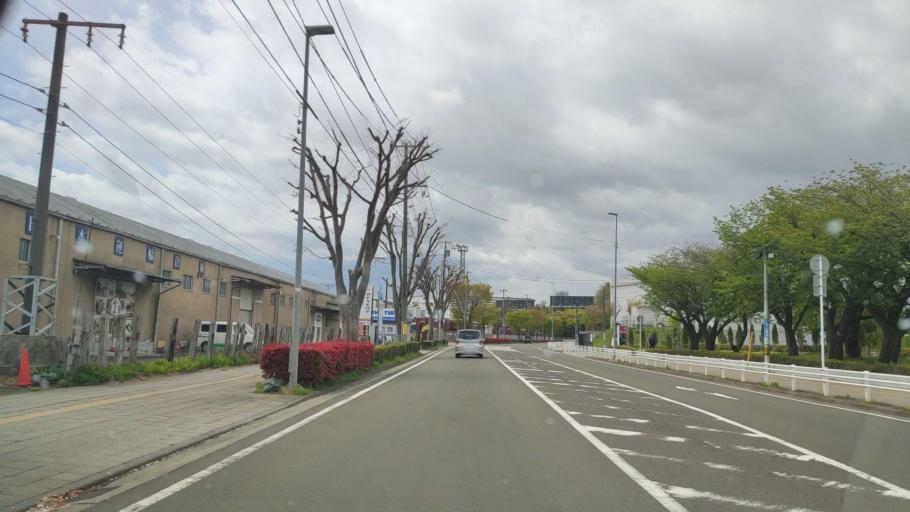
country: JP
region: Miyagi
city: Sendai-shi
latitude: 38.2590
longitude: 140.9083
